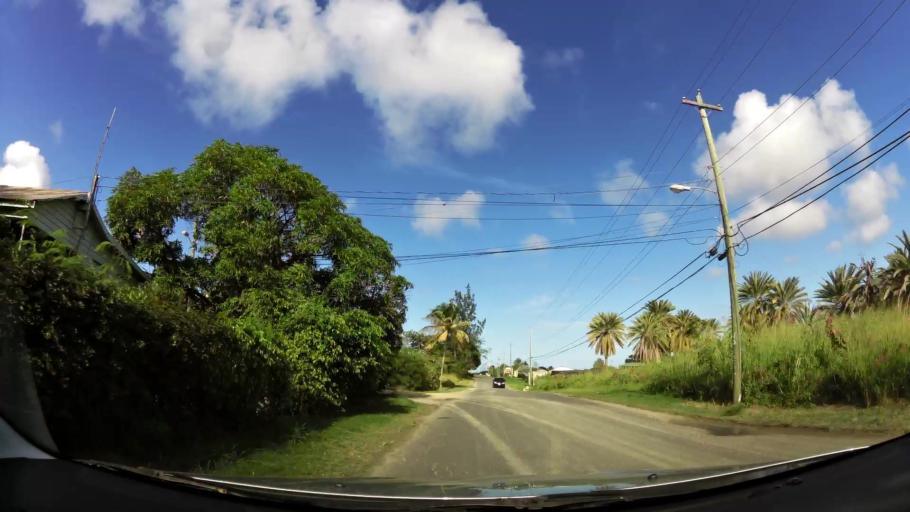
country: AG
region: Saint Peter
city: All Saints
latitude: 17.0694
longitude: -61.7907
